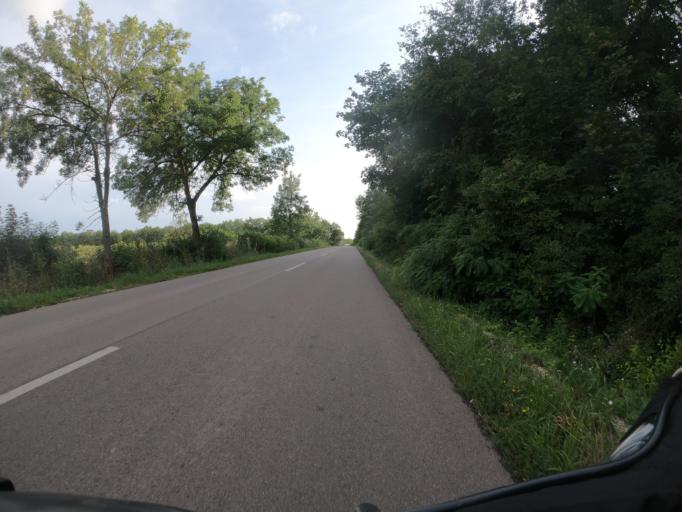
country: HU
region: Borsod-Abauj-Zemplen
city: Mezokeresztes
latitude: 47.8215
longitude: 20.7542
